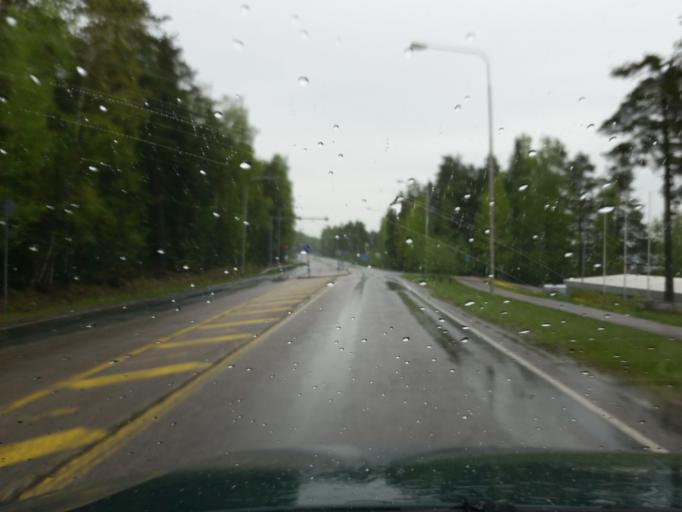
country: FI
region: Uusimaa
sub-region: Helsinki
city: Lohja
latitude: 60.2804
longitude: 24.1554
